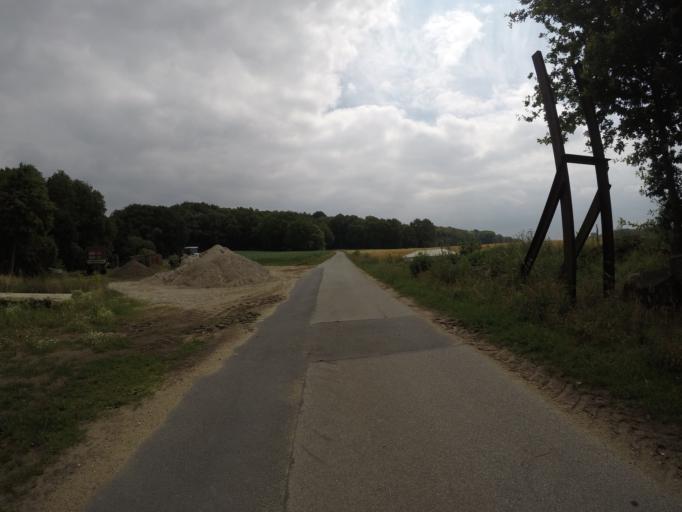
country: DE
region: North Rhine-Westphalia
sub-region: Regierungsbezirk Dusseldorf
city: Hamminkeln
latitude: 51.7348
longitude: 6.6548
